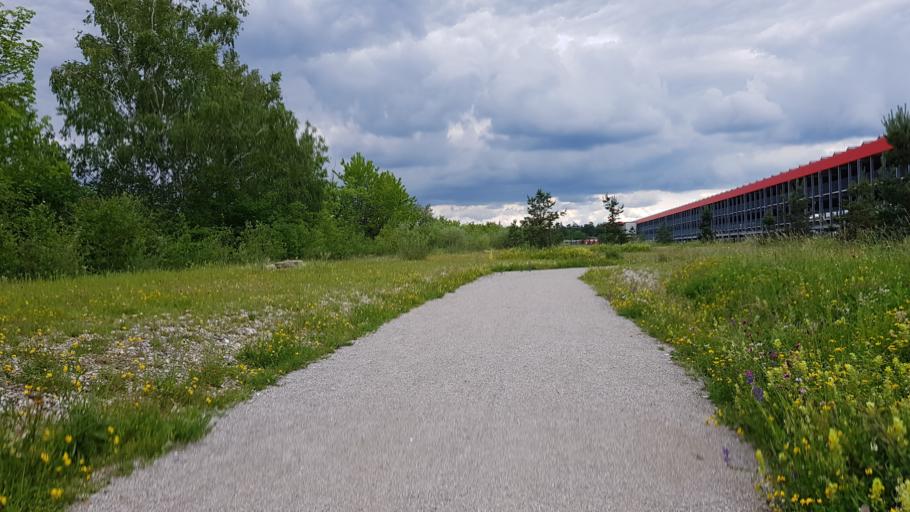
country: DE
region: Bavaria
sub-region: Upper Bavaria
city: Grafelfing
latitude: 48.1355
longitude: 11.4148
